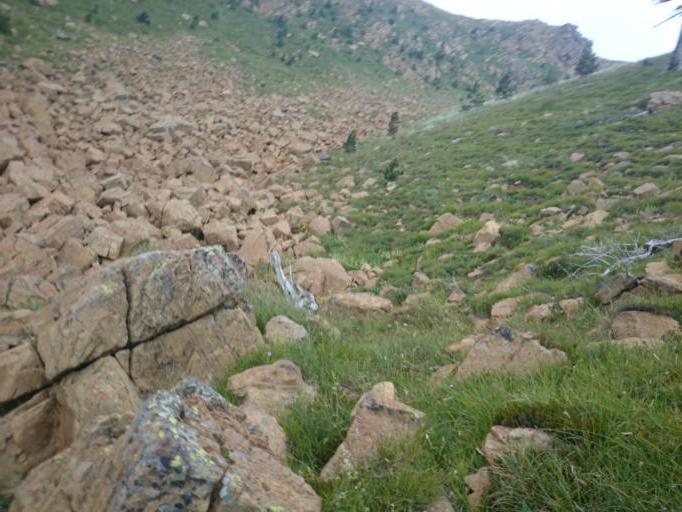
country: AL
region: Diber
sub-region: Rrethi i Dibres
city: Fushe-Lure
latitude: 41.7825
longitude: 20.1851
